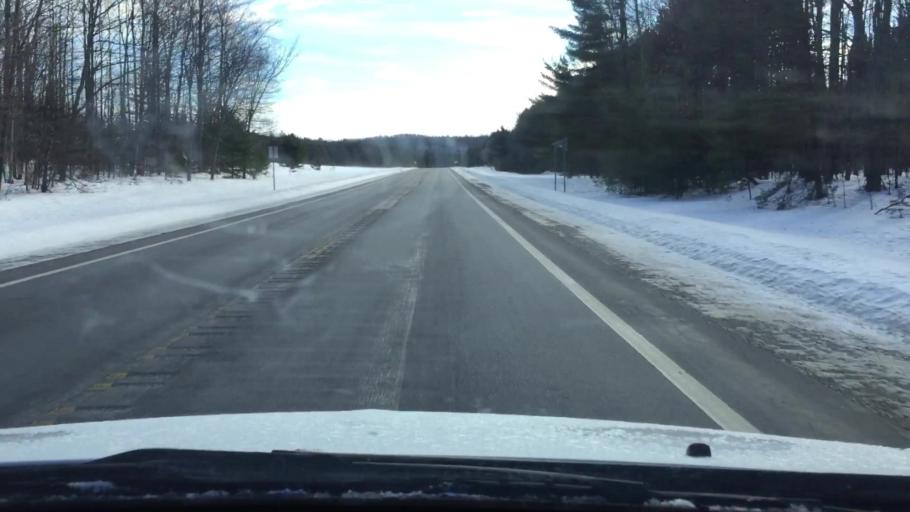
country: US
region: Michigan
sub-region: Antrim County
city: Mancelona
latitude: 44.9650
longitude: -85.0528
